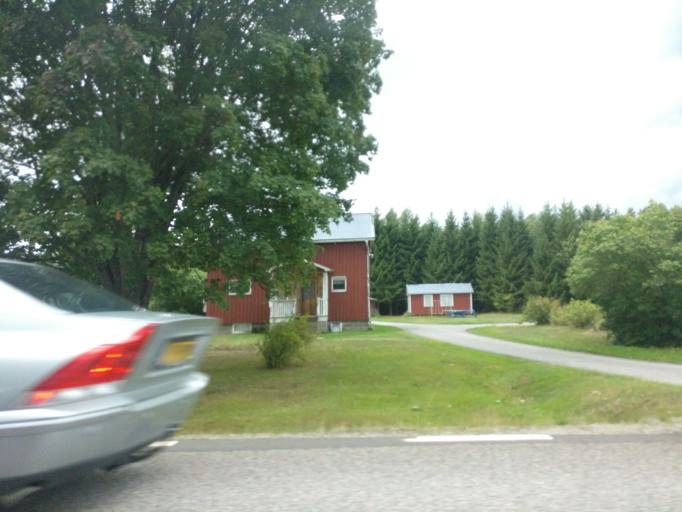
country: SE
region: Vaermland
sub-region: Torsby Kommun
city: Torsby
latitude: 60.7570
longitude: 12.7722
